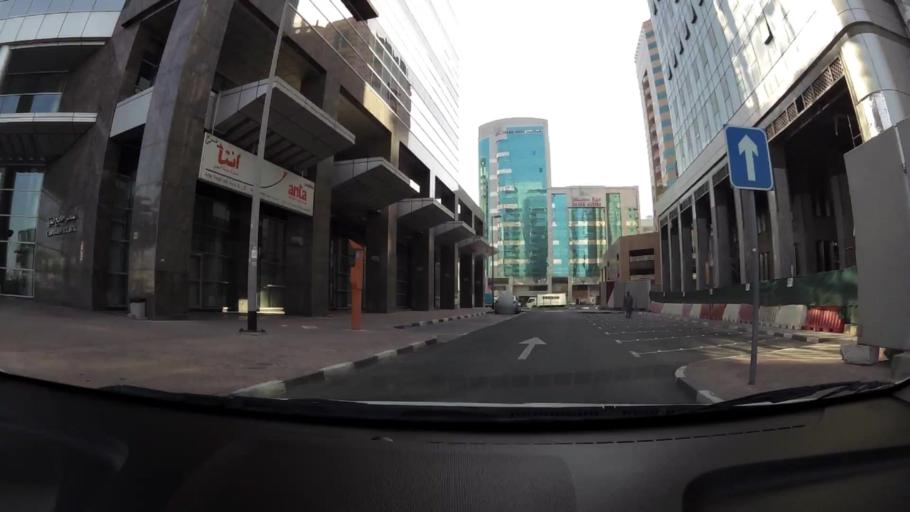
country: AE
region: Ash Shariqah
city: Sharjah
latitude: 25.2593
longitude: 55.3189
